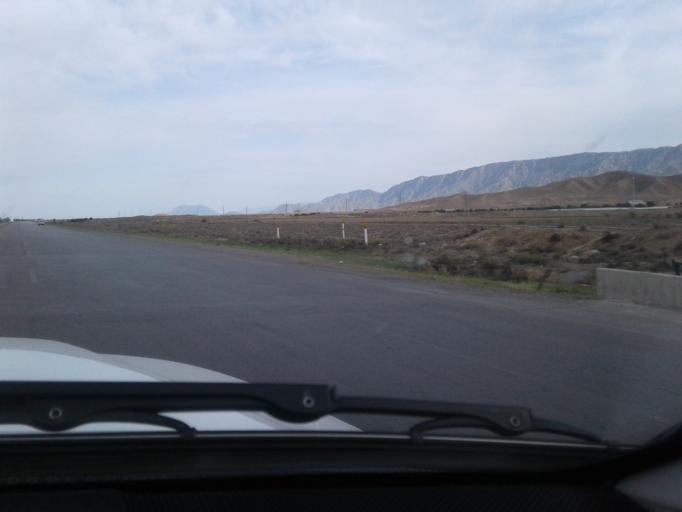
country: TM
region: Ahal
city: Baharly
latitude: 38.2402
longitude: 57.7678
